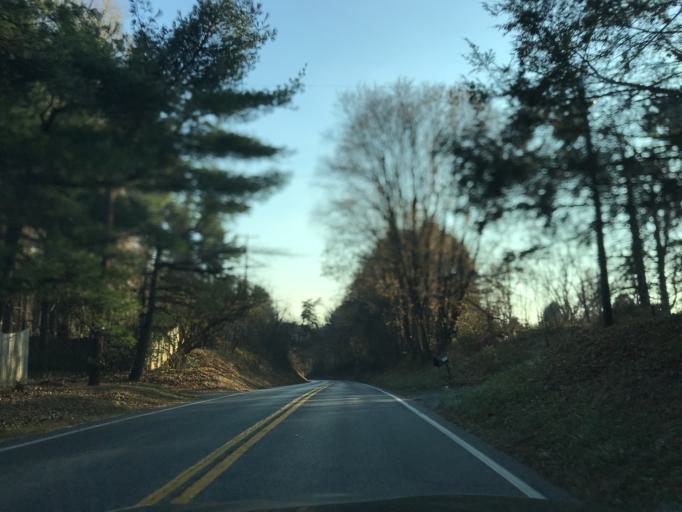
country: US
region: Maryland
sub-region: Harford County
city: Jarrettsville
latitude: 39.6008
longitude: -76.5128
